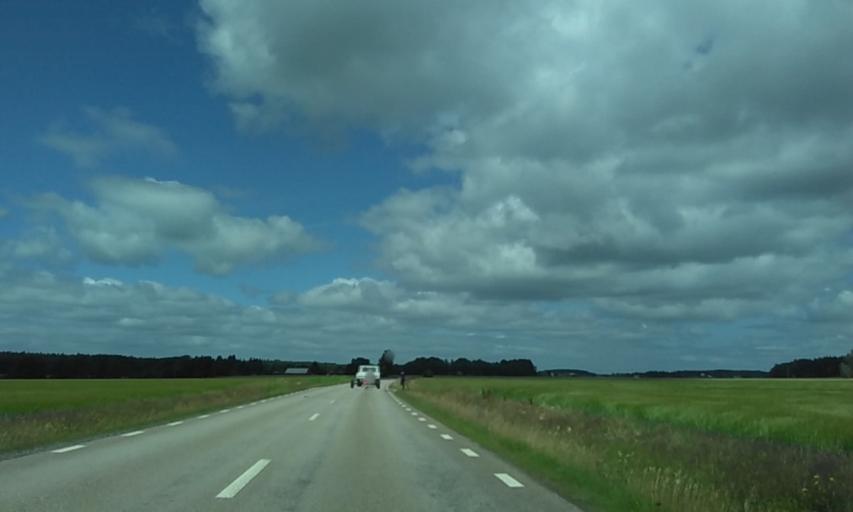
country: SE
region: Vaestra Goetaland
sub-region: Grastorps Kommun
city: Graestorp
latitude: 58.2842
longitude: 12.6727
